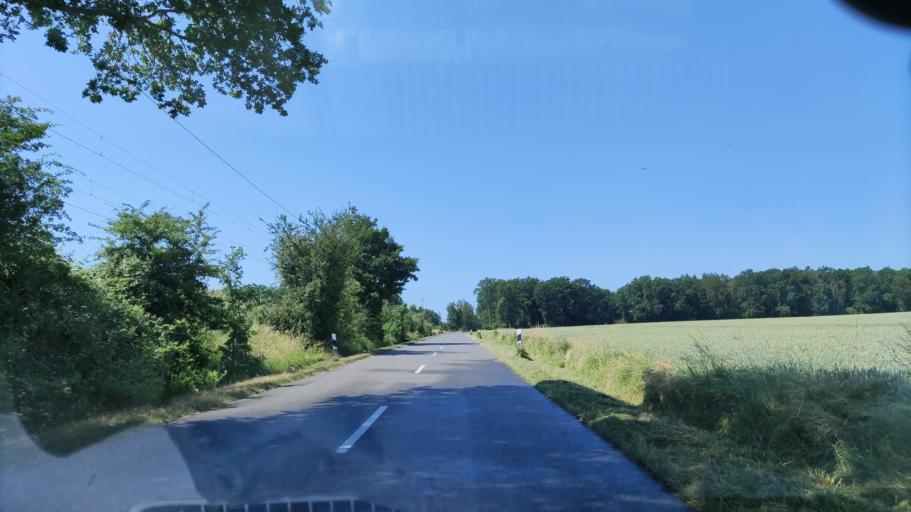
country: DE
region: Lower Saxony
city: Suderburg
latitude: 52.9236
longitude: 10.4683
